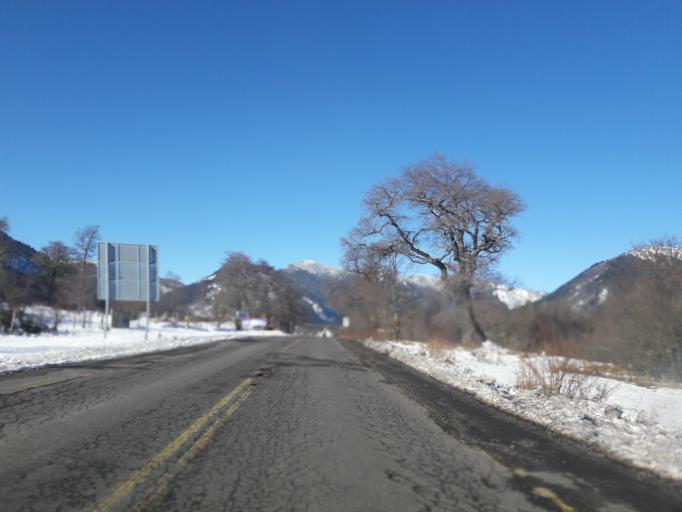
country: CL
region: Araucania
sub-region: Provincia de Cautin
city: Vilcun
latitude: -38.4725
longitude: -71.5616
